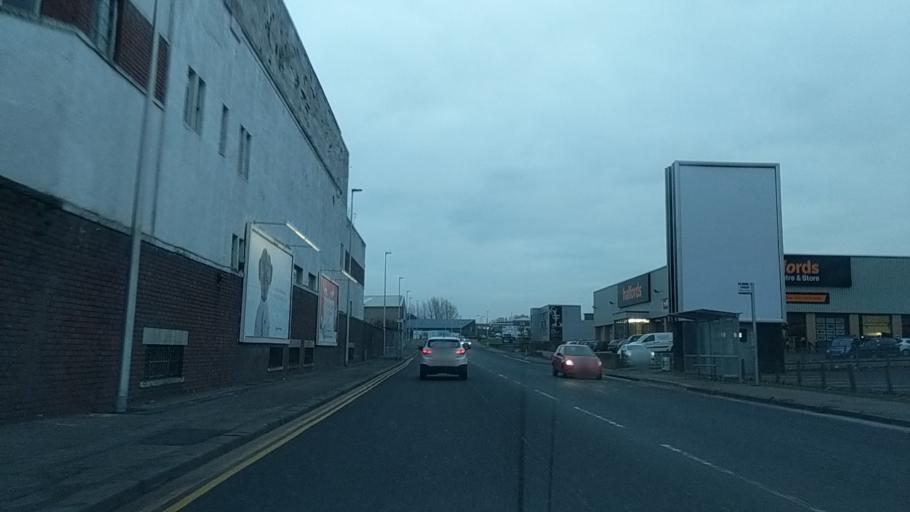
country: GB
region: Scotland
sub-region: South Lanarkshire
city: Rutherglen
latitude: 55.8376
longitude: -4.2298
